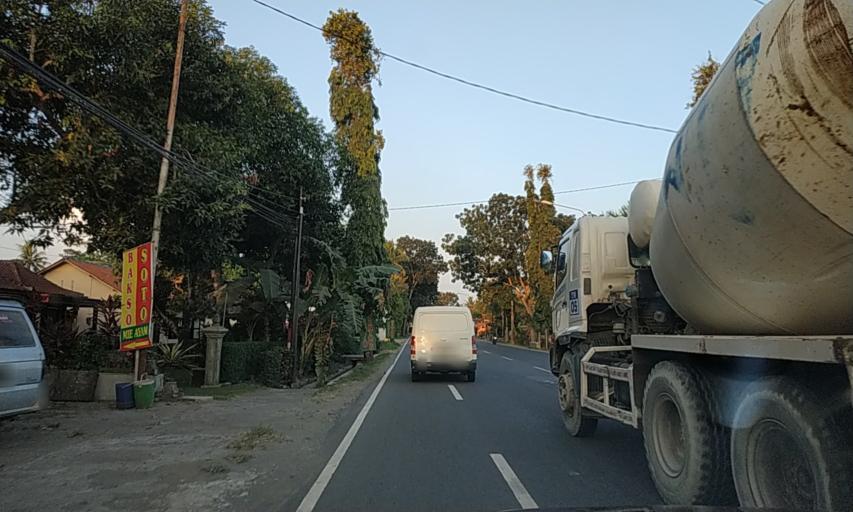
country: ID
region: Daerah Istimewa Yogyakarta
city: Srandakan
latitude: -7.8869
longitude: 110.0785
